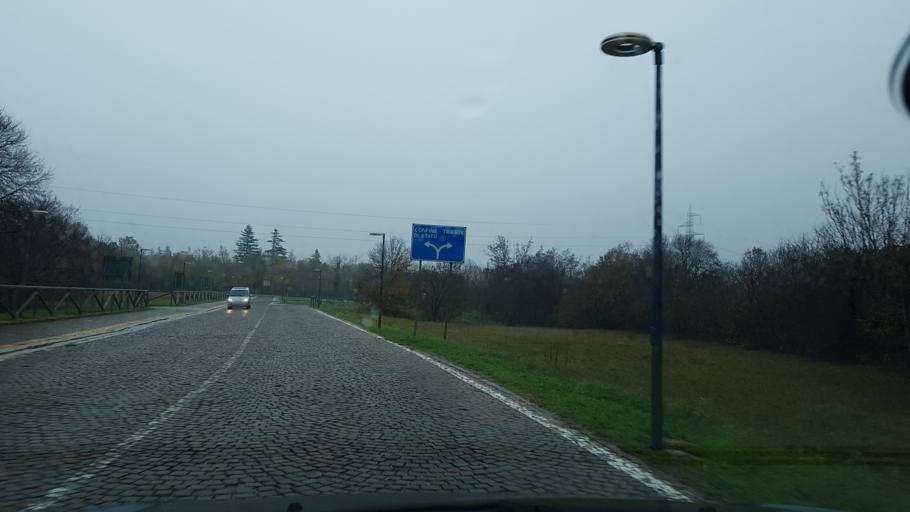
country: IT
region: Friuli Venezia Giulia
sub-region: Provincia di Trieste
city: Domio
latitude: 45.6404
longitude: 13.8536
